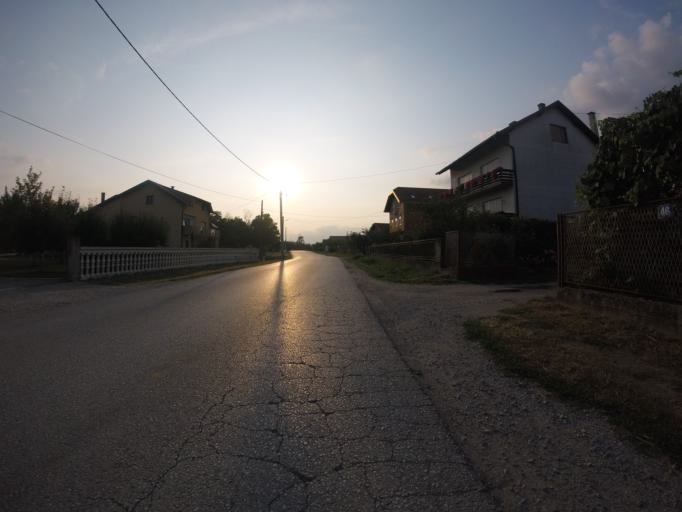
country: HR
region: Zagrebacka
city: Micevec
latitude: 45.7508
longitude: 16.1191
